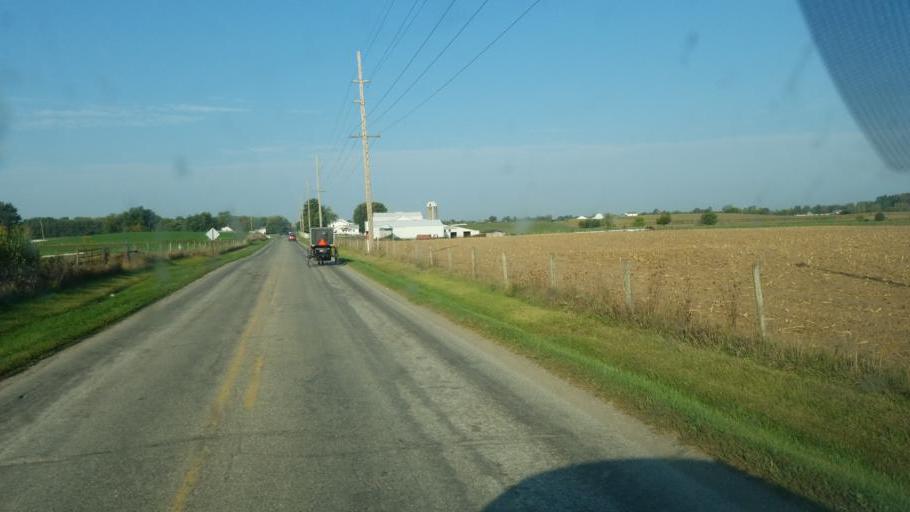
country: US
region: Indiana
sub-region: LaGrange County
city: Topeka
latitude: 41.6766
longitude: -85.5576
